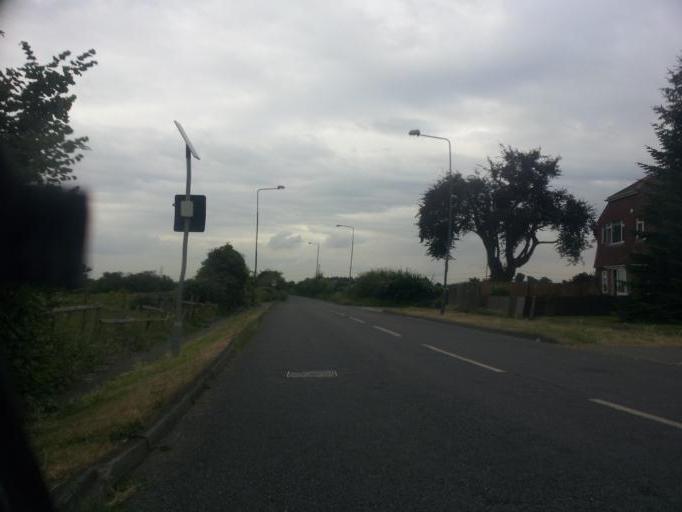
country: GB
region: England
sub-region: Kent
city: Gravesend
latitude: 51.4331
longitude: 0.4121
